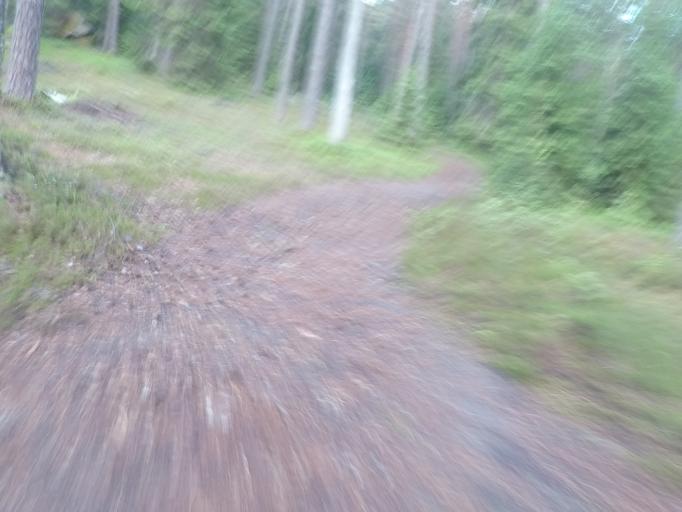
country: SE
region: Soedermanland
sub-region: Eskilstuna Kommun
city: Hallbybrunn
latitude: 59.3952
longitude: 16.4020
